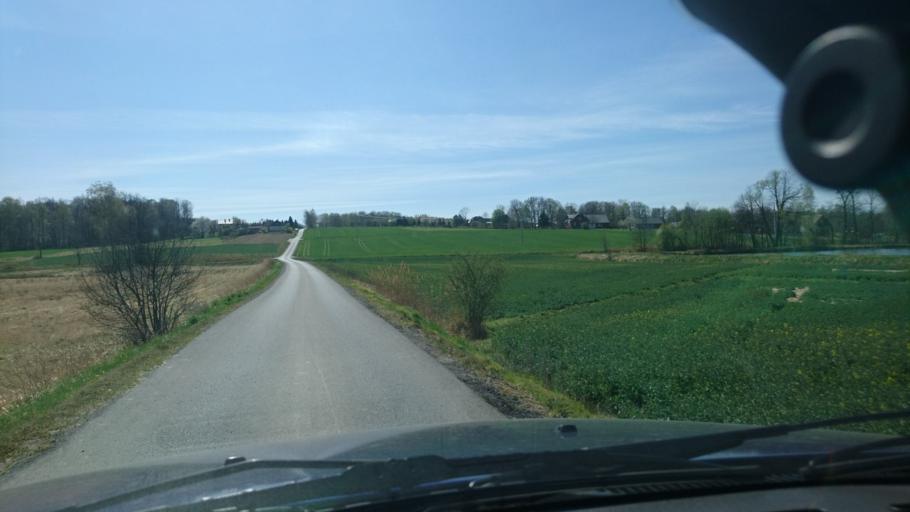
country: PL
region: Silesian Voivodeship
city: Janowice
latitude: 49.8938
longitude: 19.1055
